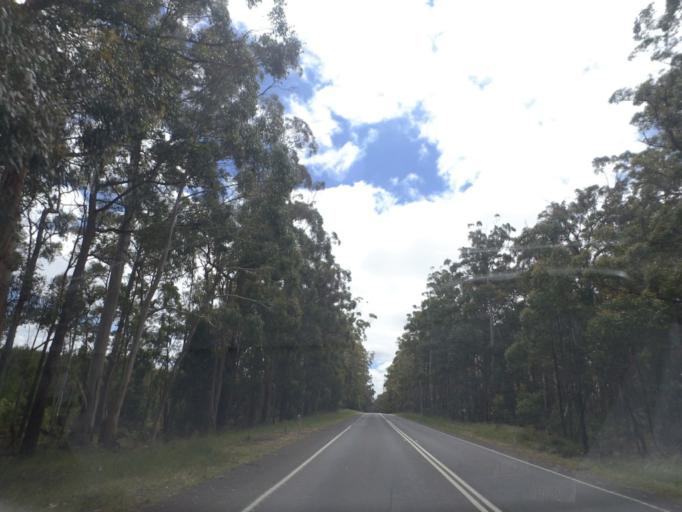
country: AU
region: Victoria
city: Brown Hill
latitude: -37.4978
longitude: 144.1552
